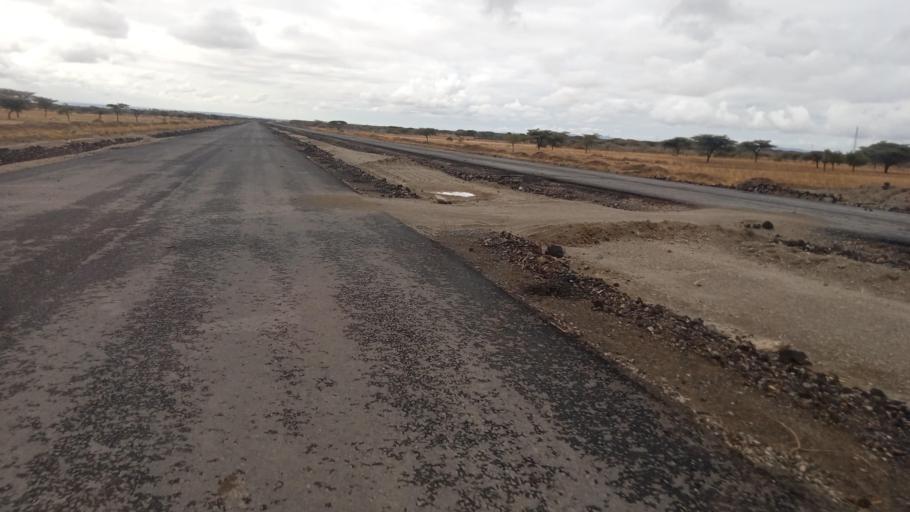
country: ET
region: Oromiya
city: Ziway
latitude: 7.6113
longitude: 38.6790
